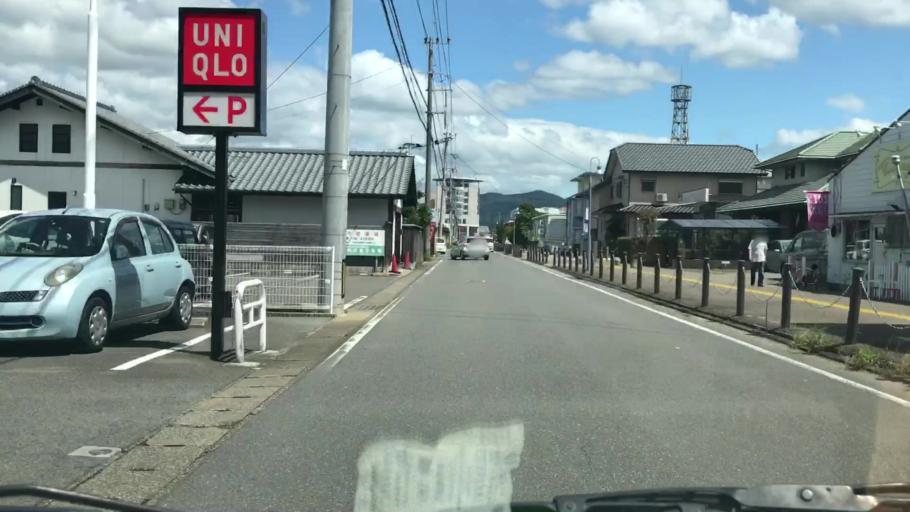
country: JP
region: Saga Prefecture
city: Takeocho-takeo
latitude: 33.1949
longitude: 130.0306
